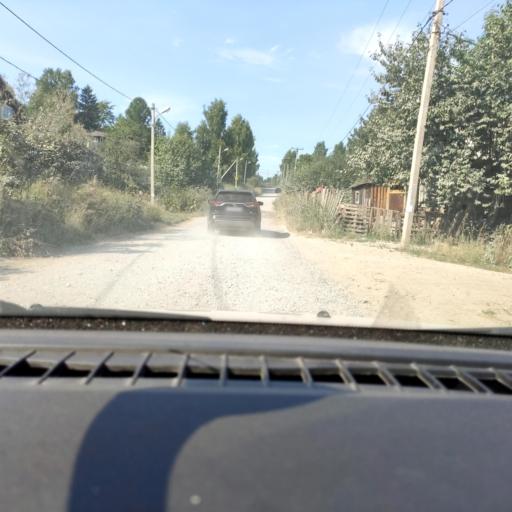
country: RU
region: Perm
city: Polazna
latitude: 58.1372
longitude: 56.4573
